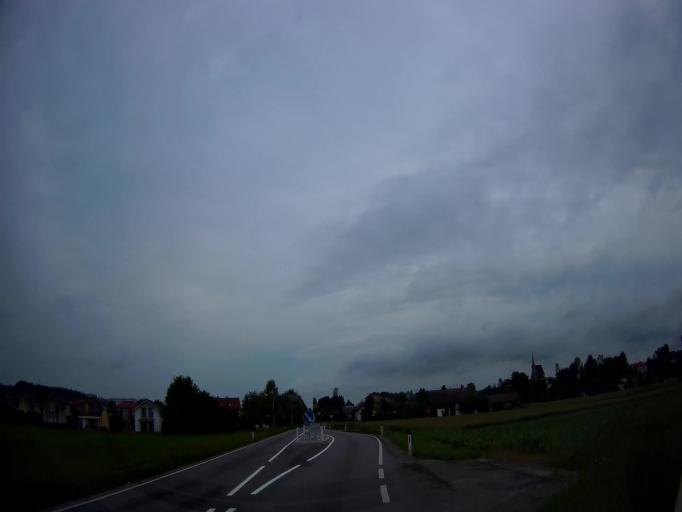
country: AT
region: Salzburg
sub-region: Politischer Bezirk Salzburg-Umgebung
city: Mattsee
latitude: 48.0716
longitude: 13.1424
